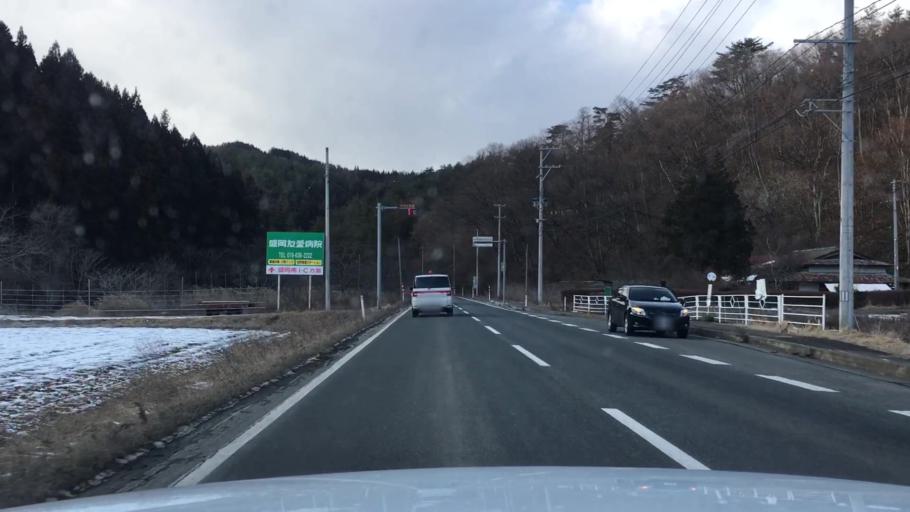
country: JP
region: Iwate
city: Morioka-shi
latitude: 39.6753
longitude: 141.2281
